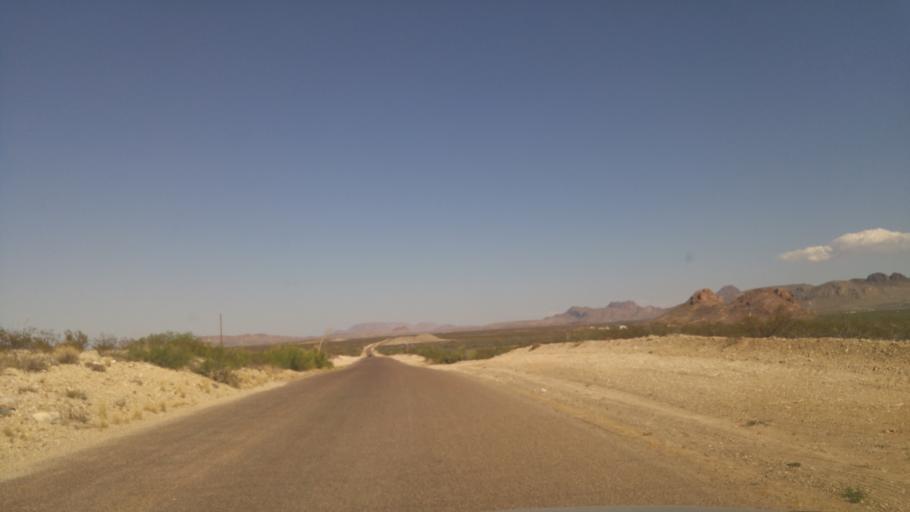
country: US
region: Texas
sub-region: Brewster County
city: Alpine
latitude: 29.5485
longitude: -103.5310
